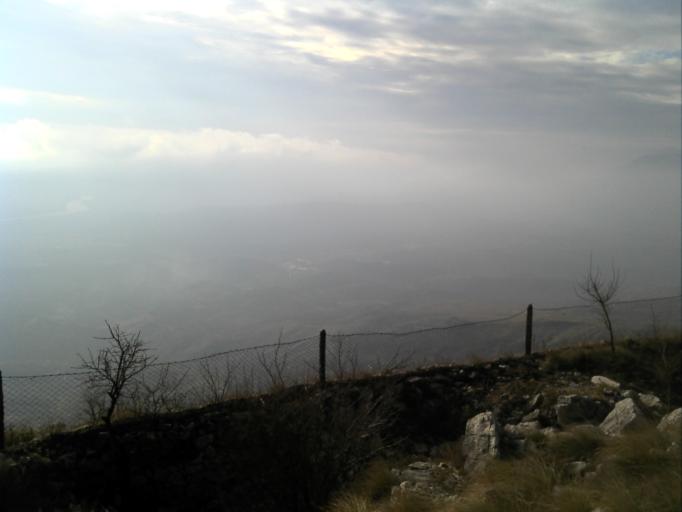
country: AL
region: Shkoder
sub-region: Rrethi i Shkodres
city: Berdica e Madhe
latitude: 42.0467
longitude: 19.4485
